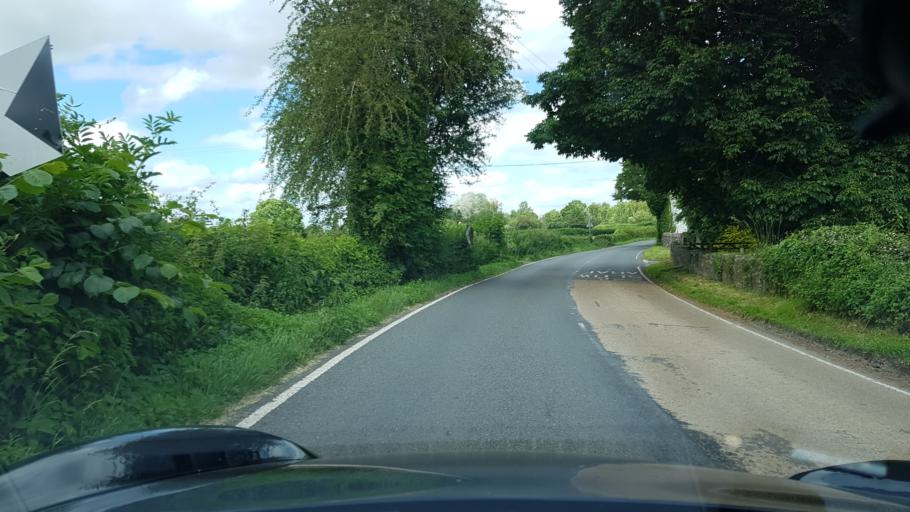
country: GB
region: Wales
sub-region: Monmouthshire
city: Llanarth
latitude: 51.7457
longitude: -2.9486
